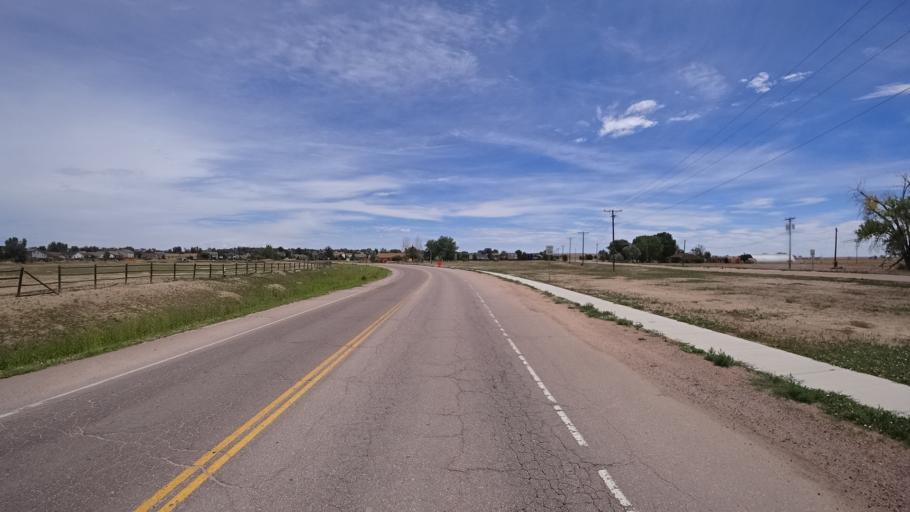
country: US
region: Colorado
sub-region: El Paso County
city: Fountain
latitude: 38.6649
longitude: -104.6843
